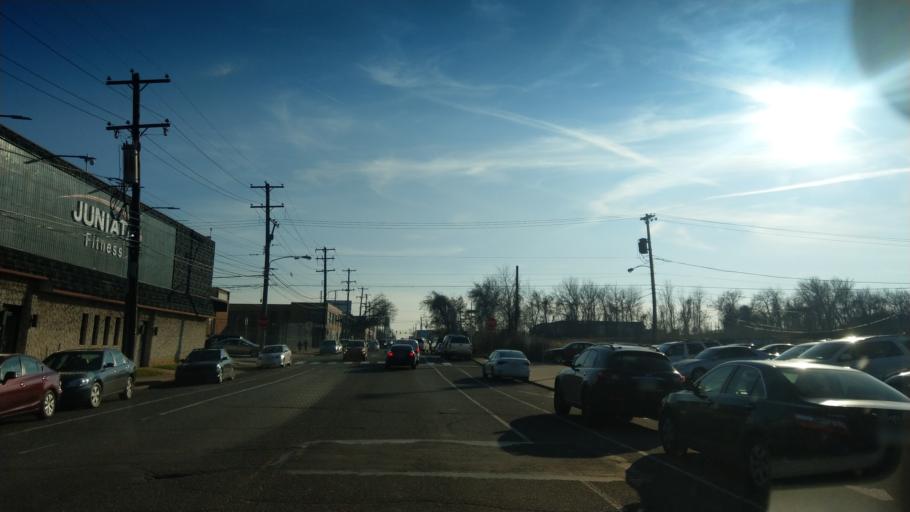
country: US
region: Pennsylvania
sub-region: Montgomery County
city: Rockledge
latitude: 40.0158
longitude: -75.1114
